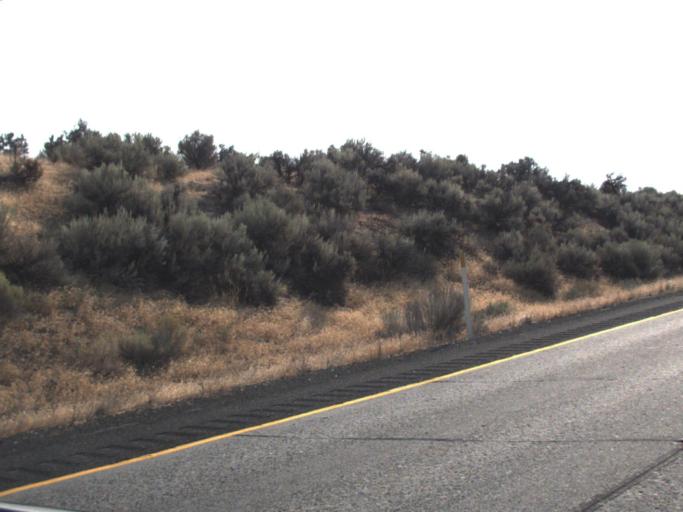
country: US
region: Washington
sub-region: Kittitas County
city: Kittitas
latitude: 46.9069
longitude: -120.4629
